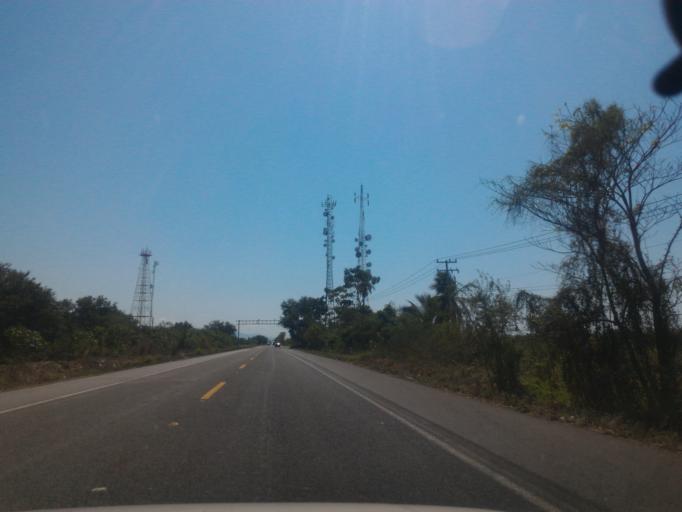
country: MX
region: Colima
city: Tecoman
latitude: 18.8292
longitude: -103.8151
